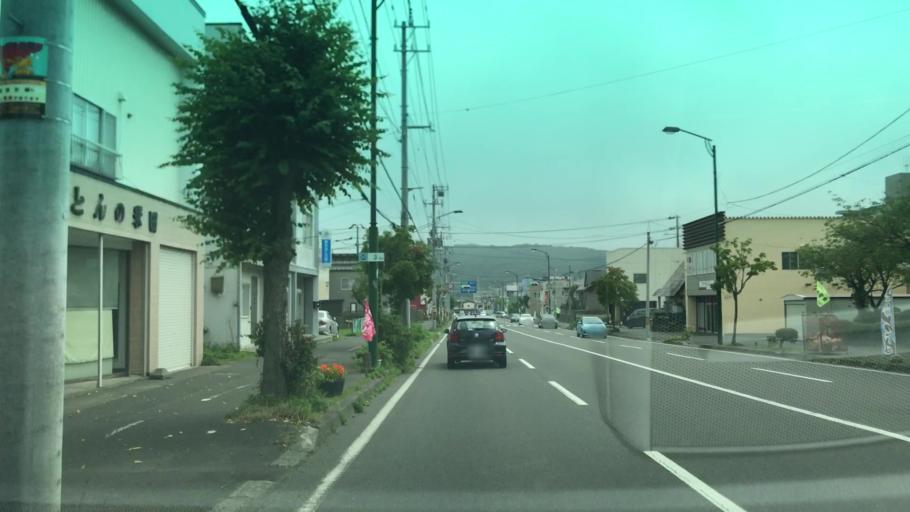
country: JP
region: Hokkaido
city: Muroran
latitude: 42.3628
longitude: 141.0393
